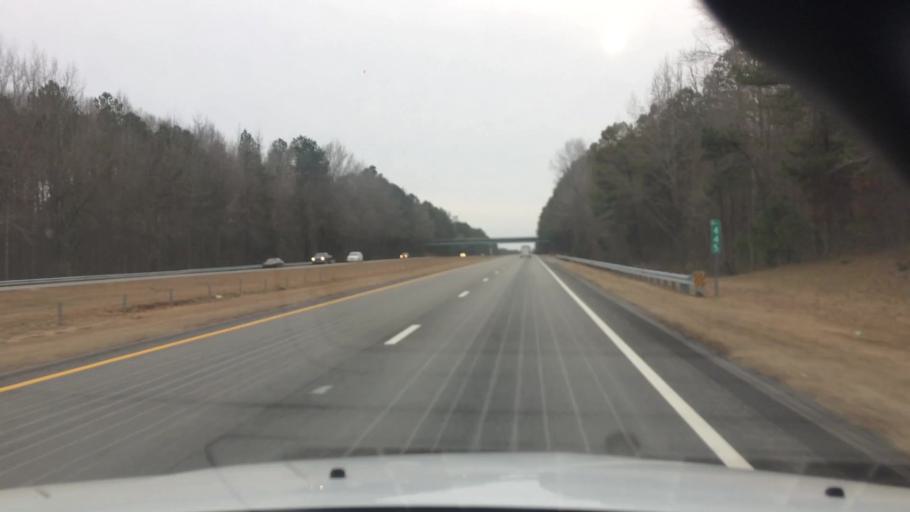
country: US
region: North Carolina
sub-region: Nash County
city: Spring Hope
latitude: 35.9032
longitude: -78.1820
